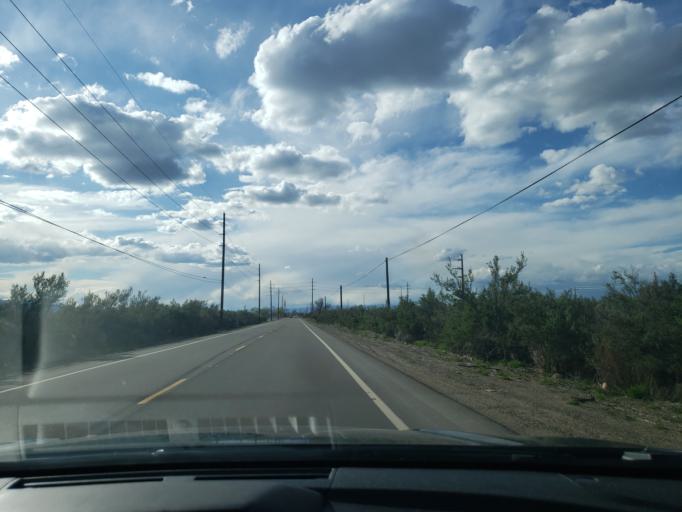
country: US
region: Colorado
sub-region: Mesa County
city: Redlands
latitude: 39.1132
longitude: -108.6523
